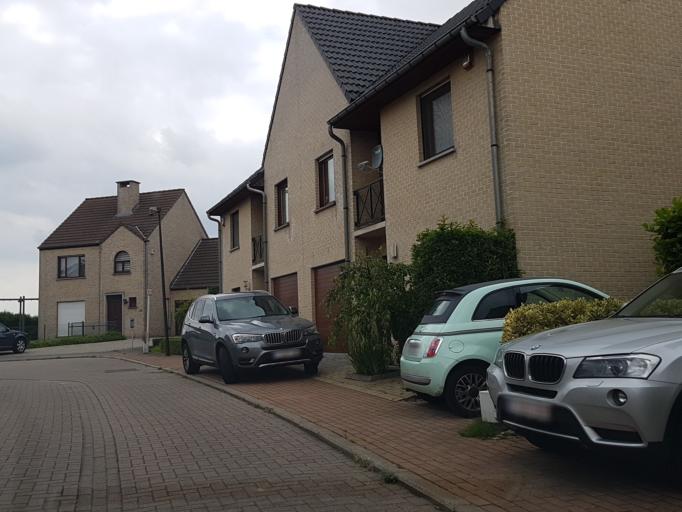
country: BE
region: Flanders
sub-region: Provincie Vlaams-Brabant
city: Kraainem
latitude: 50.8738
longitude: 4.4505
